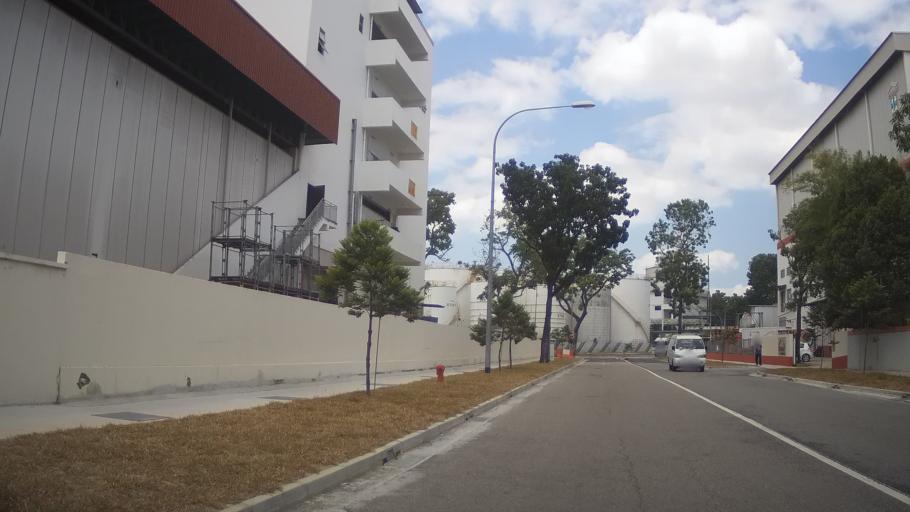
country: SG
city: Singapore
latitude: 1.3104
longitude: 103.7223
